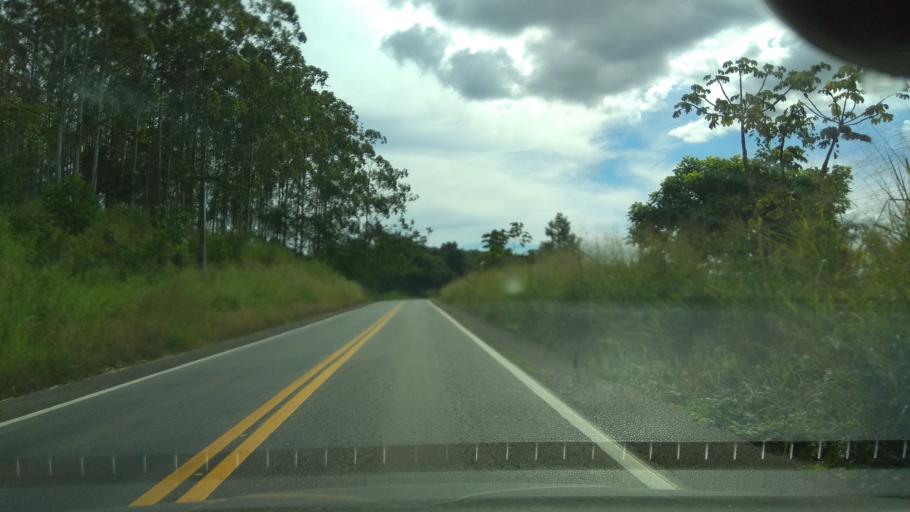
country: BR
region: Bahia
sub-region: Ipiau
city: Ipiau
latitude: -14.0736
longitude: -39.7867
